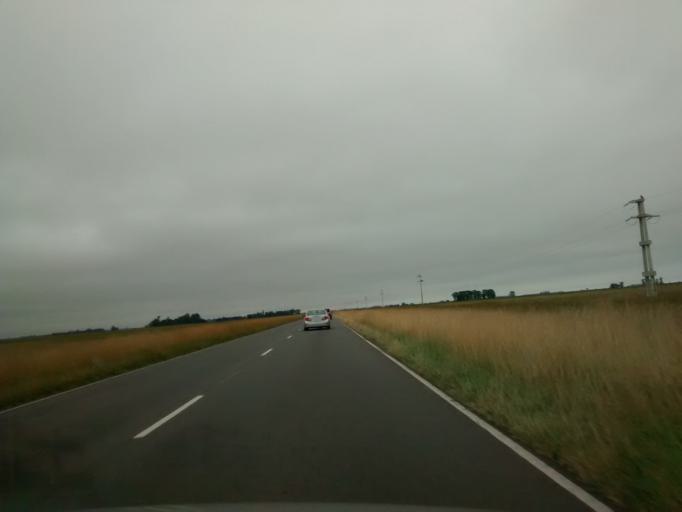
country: AR
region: Buenos Aires
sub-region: Partido de Ayacucho
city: Ayacucho
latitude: -37.0332
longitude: -58.5400
